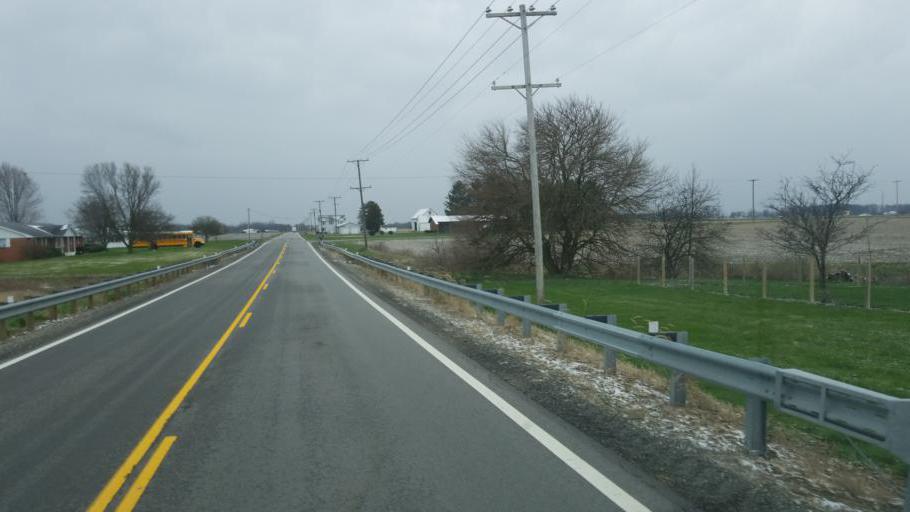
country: US
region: Ohio
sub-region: Marion County
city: Marion
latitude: 40.4854
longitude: -83.0686
